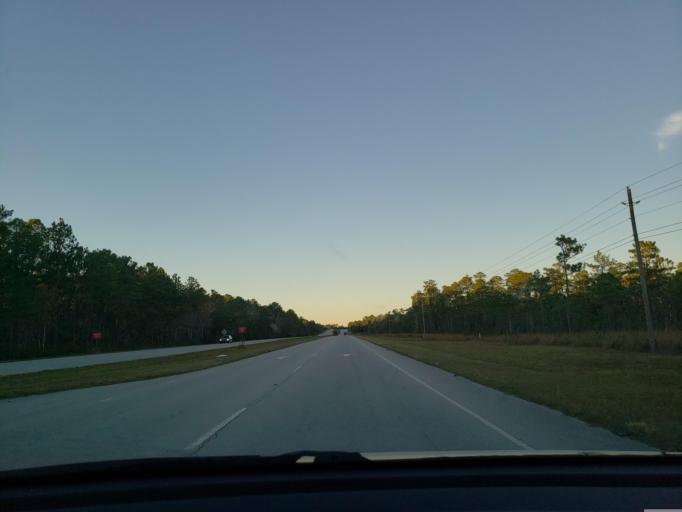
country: US
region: North Carolina
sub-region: Onslow County
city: Sneads Ferry
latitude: 34.6046
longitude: -77.4823
